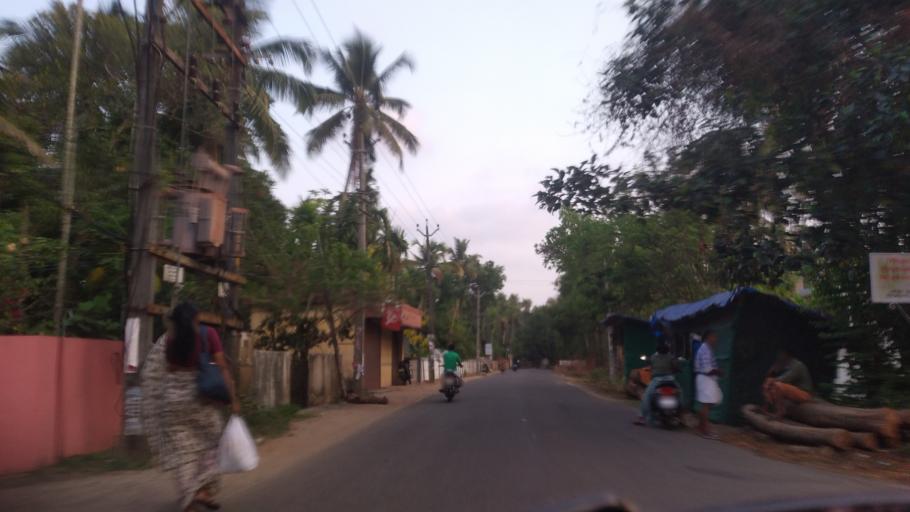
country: IN
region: Kerala
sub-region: Thrissur District
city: Kodungallur
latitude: 10.2327
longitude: 76.1540
